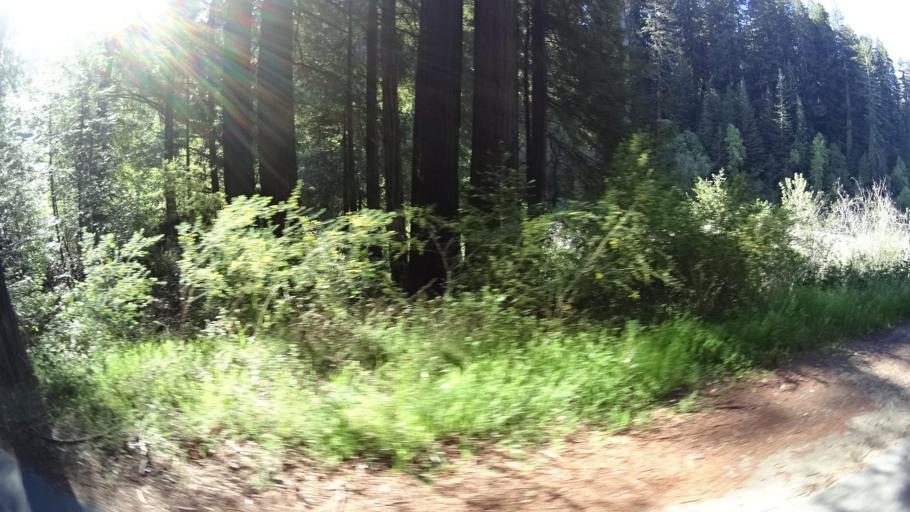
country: US
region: California
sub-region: Humboldt County
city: Rio Dell
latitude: 40.3450
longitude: -123.9352
